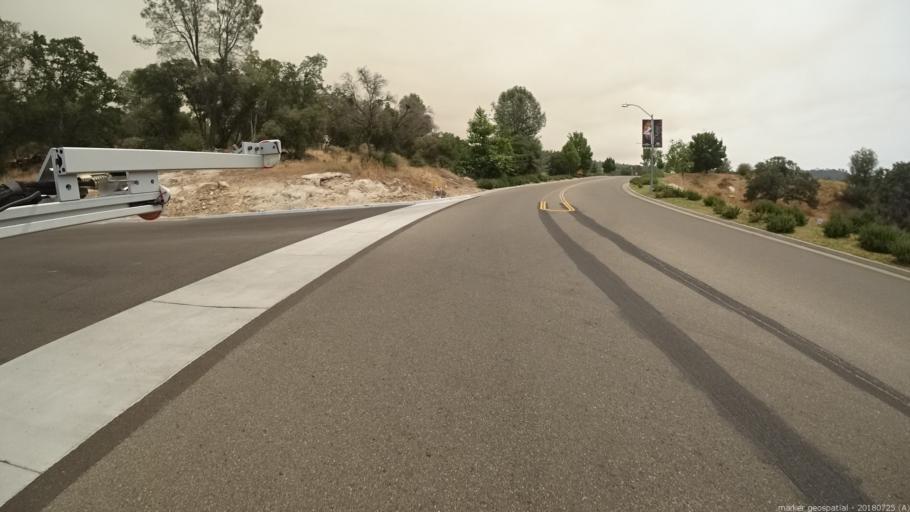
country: US
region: California
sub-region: Madera County
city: Coarsegold
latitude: 37.2131
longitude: -119.7065
